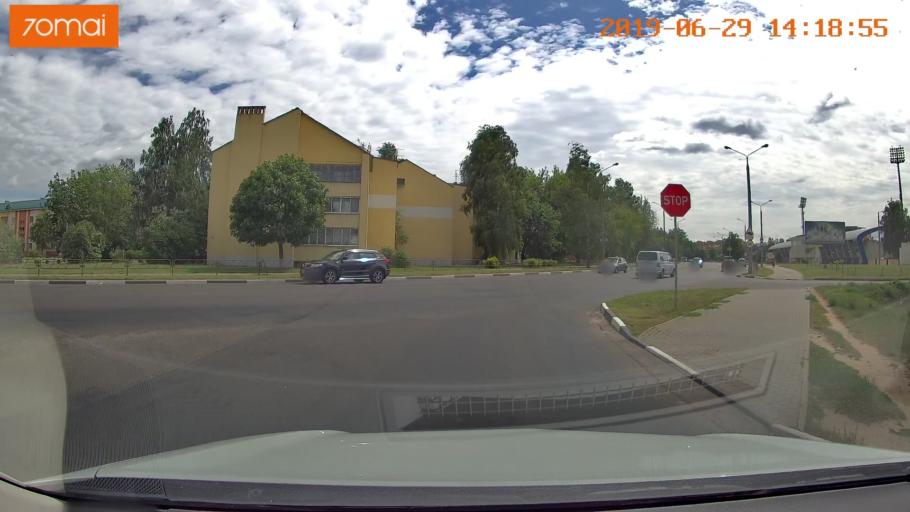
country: BY
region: Minsk
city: Salihorsk
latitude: 52.8011
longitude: 27.5403
